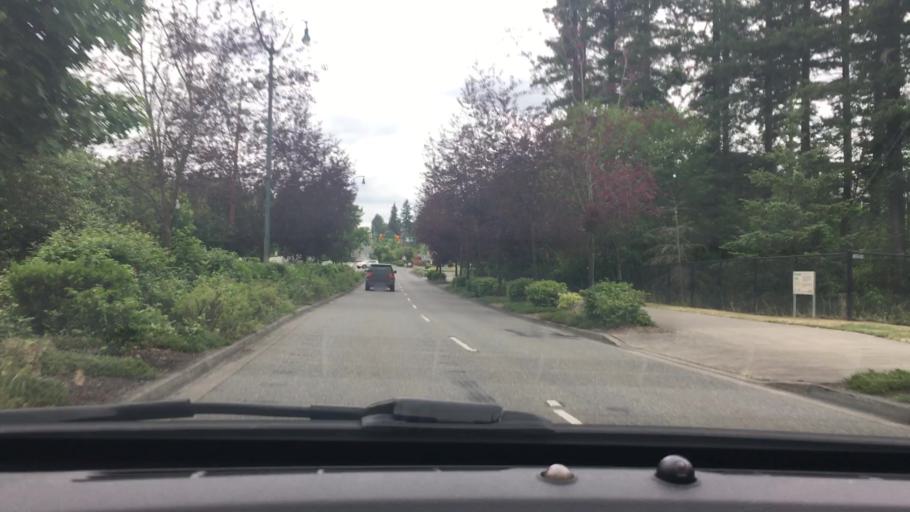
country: US
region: Washington
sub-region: King County
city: City of Sammamish
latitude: 47.6115
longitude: -122.0354
